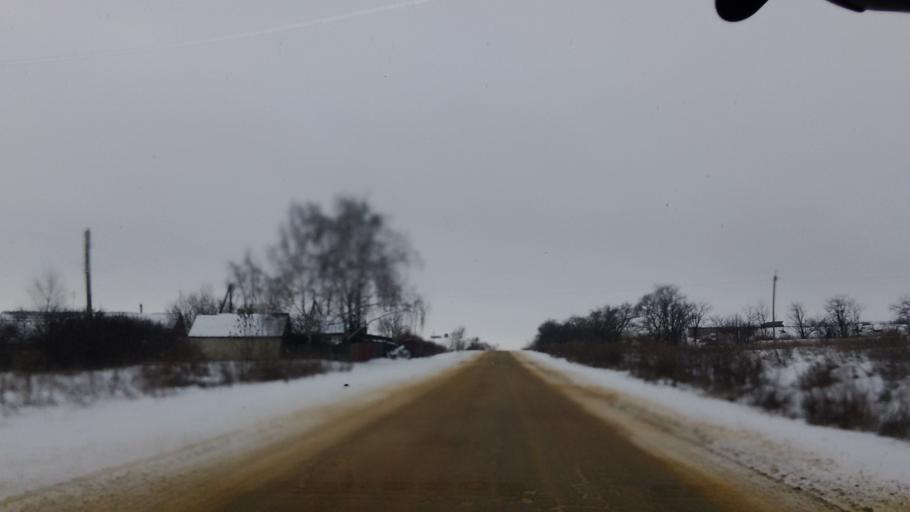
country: RU
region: Tula
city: Bogoroditsk
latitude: 53.7565
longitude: 37.9875
